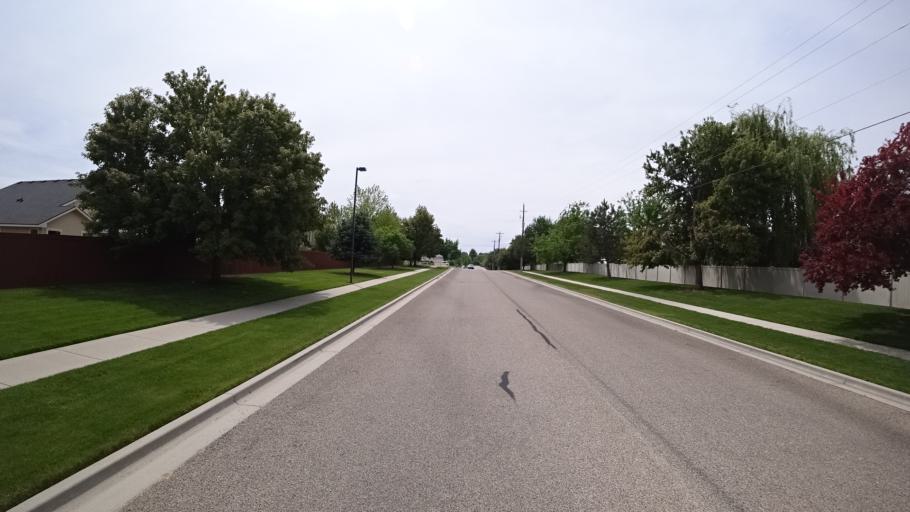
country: US
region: Idaho
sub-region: Ada County
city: Meridian
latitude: 43.5479
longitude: -116.3243
